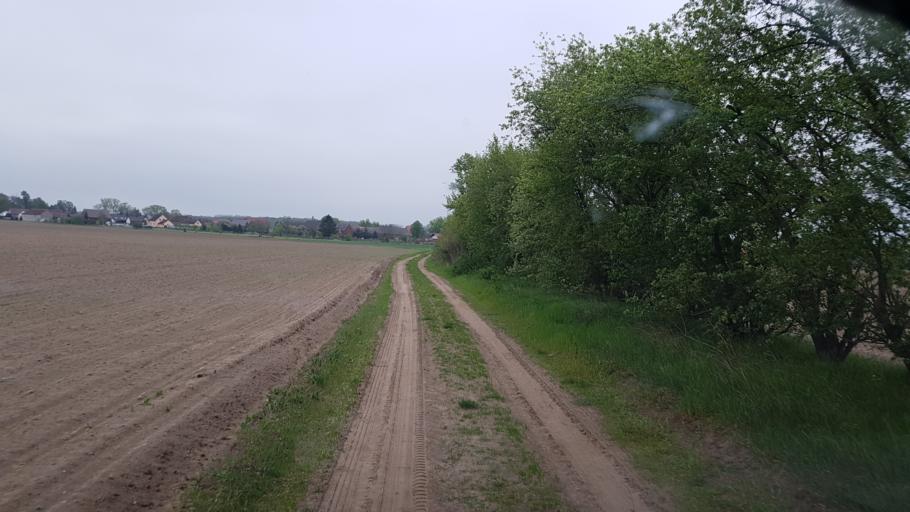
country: DE
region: Brandenburg
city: Schonewalde
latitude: 51.7010
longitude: 13.5644
